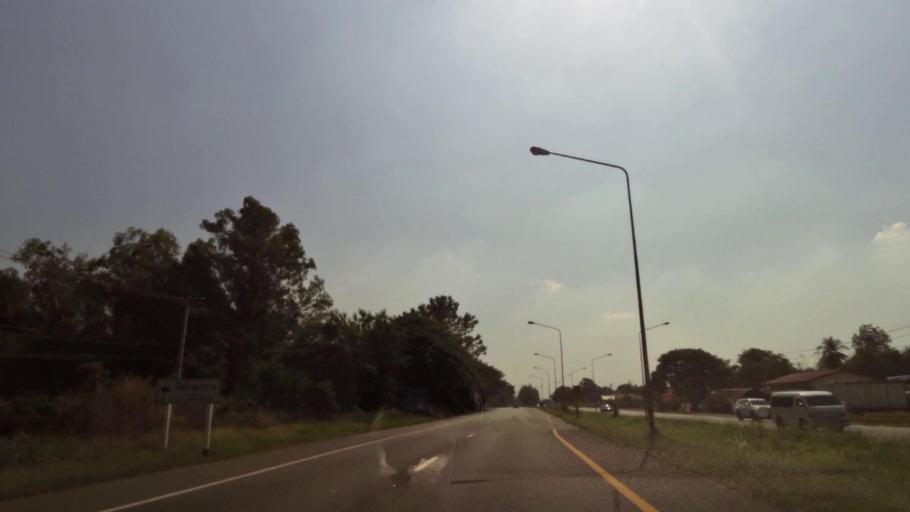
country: TH
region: Phichit
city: Bueng Na Rang
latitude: 16.1954
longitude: 100.1284
